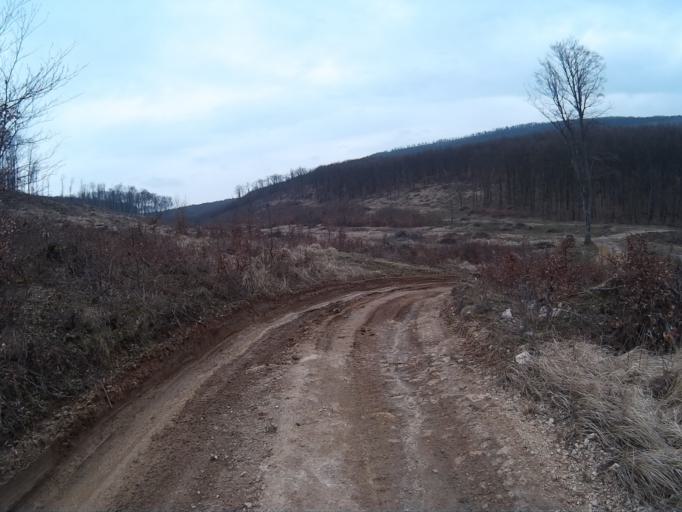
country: HU
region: Veszprem
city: Zirc
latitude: 47.1877
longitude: 17.8984
